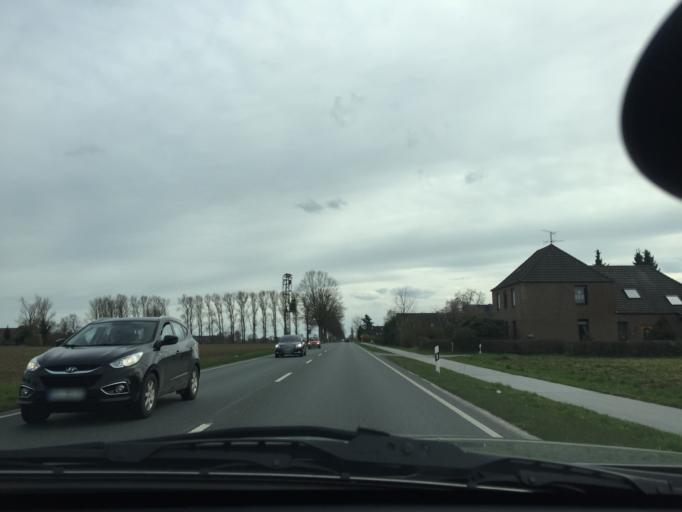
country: DE
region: North Rhine-Westphalia
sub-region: Regierungsbezirk Dusseldorf
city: Goch
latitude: 51.7331
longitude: 6.1596
